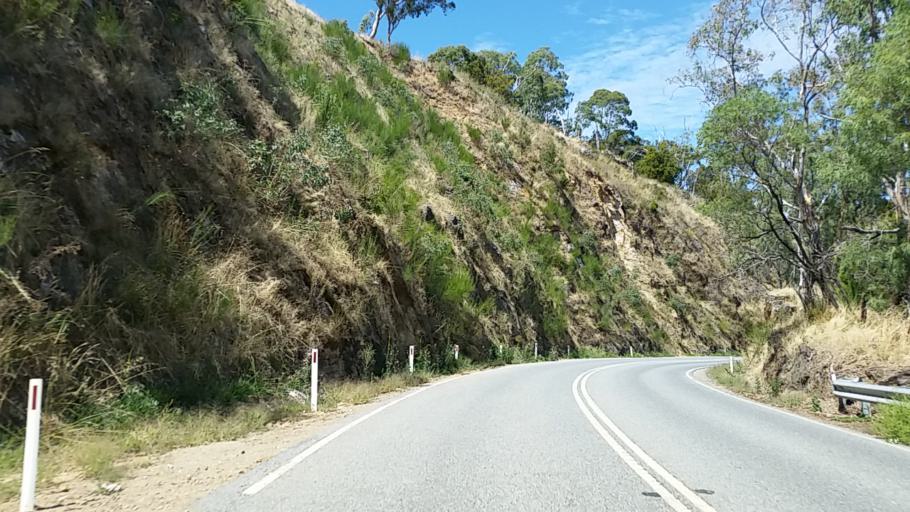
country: AU
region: South Australia
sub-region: Tea Tree Gully
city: Golden Grove
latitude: -34.8488
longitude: 138.7957
